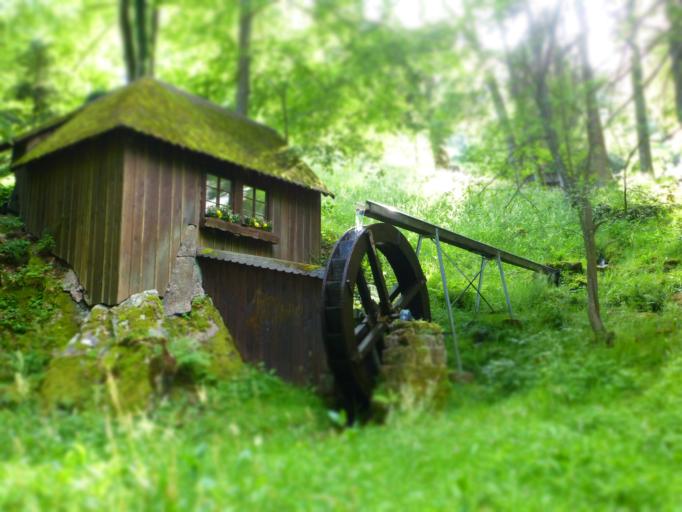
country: DE
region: Baden-Wuerttemberg
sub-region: Karlsruhe Region
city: Bad Wildbad
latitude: 48.7461
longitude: 8.5465
